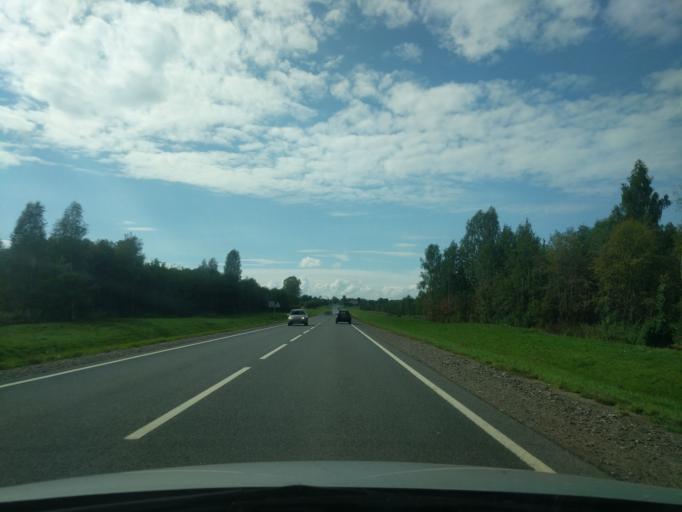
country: RU
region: Kostroma
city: Oktyabr'skiy
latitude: 57.7979
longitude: 41.2220
